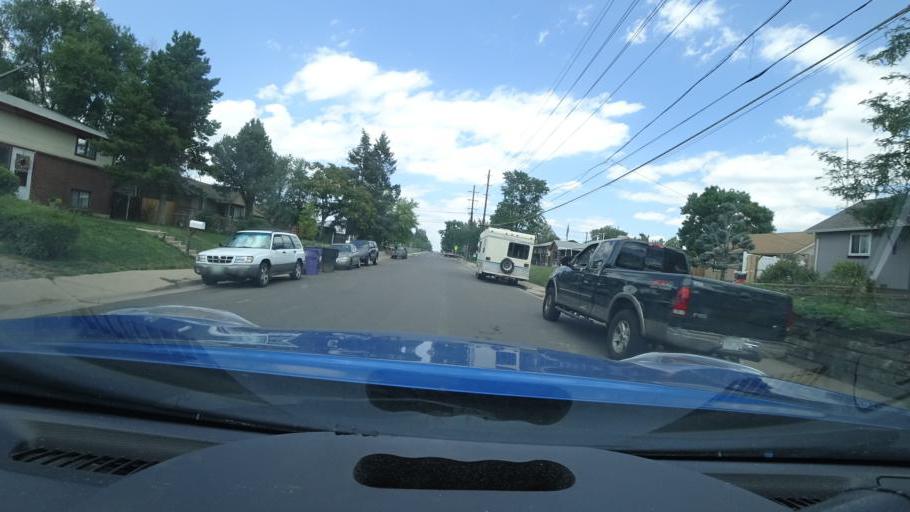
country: US
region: Colorado
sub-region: Arapahoe County
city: Sheridan
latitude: 39.6813
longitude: -105.0110
